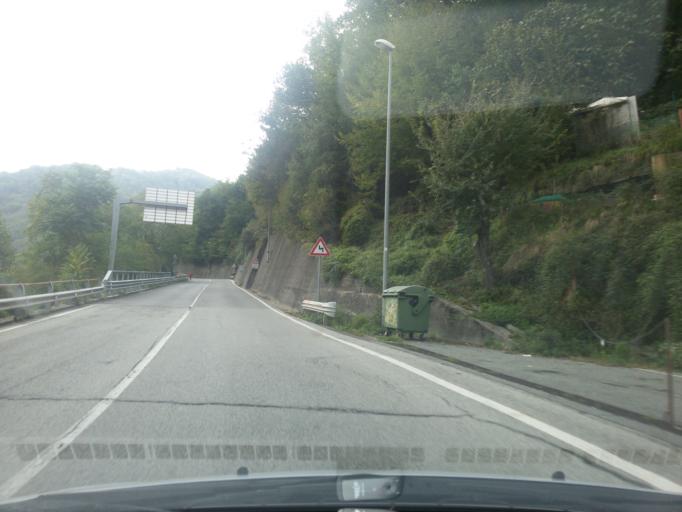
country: IT
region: Liguria
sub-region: Provincia di Genova
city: Bargagli
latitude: 44.4434
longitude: 9.0912
